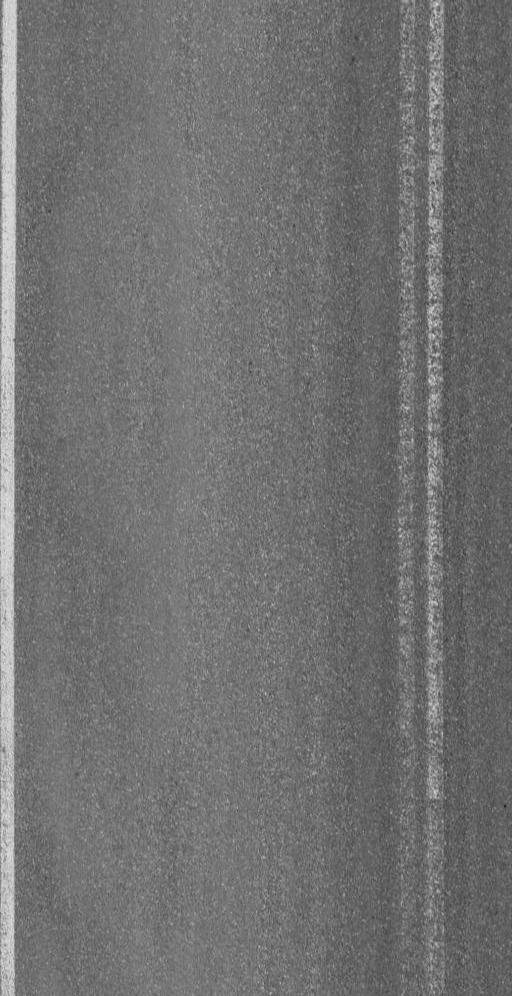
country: US
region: Vermont
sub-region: Washington County
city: South Barre
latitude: 44.1765
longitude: -72.4610
